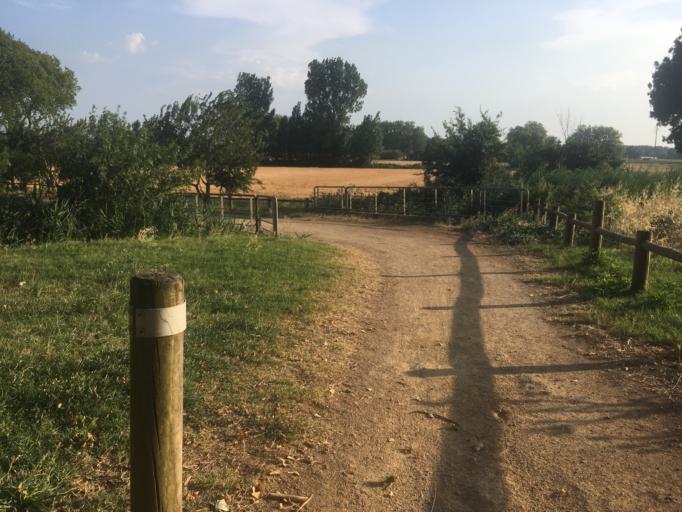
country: FR
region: Languedoc-Roussillon
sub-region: Departement de l'Aude
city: Bram
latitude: 43.2554
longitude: 2.1258
